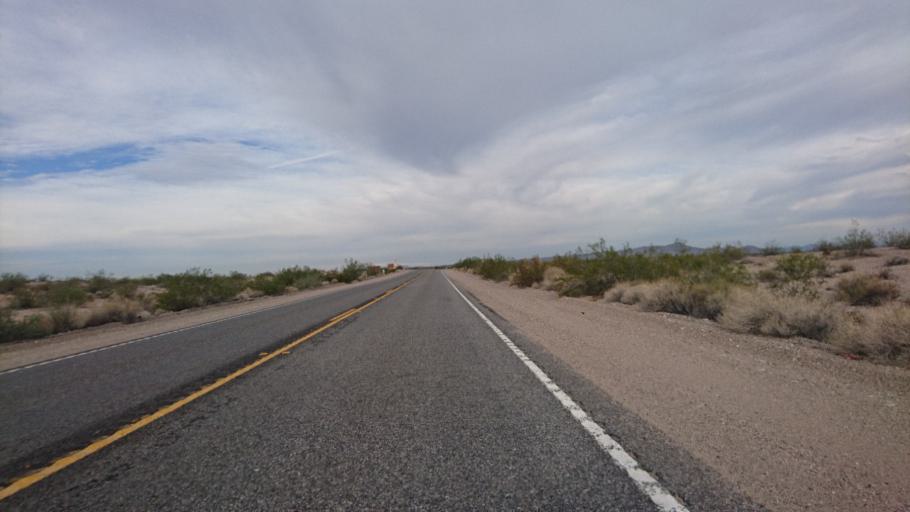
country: US
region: Arizona
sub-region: Mohave County
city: Willow Valley
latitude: 34.9351
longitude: -114.8034
